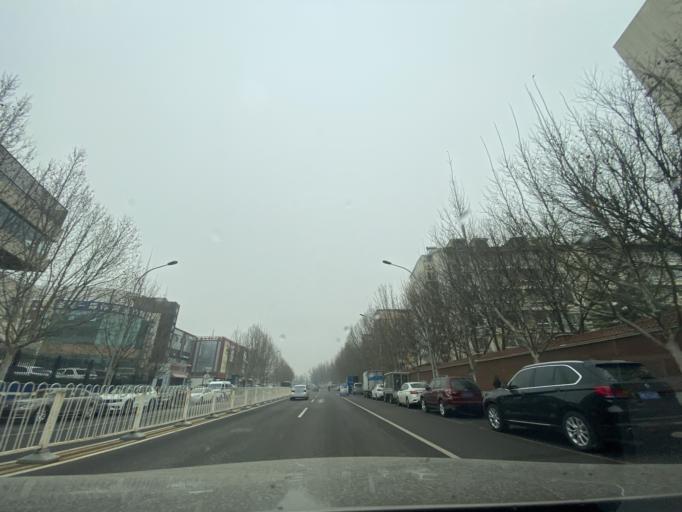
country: CN
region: Beijing
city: Sijiqing
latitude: 39.9646
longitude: 116.2417
